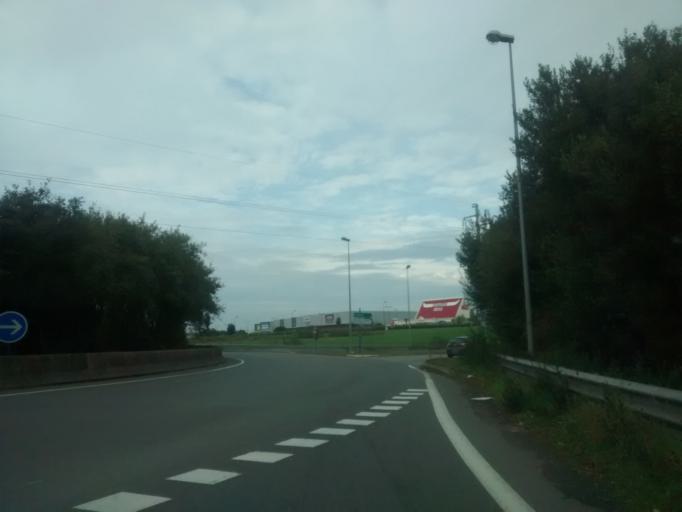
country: FR
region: Brittany
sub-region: Departement d'Ille-et-Vilaine
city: Dinard
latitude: 48.6135
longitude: -2.0568
